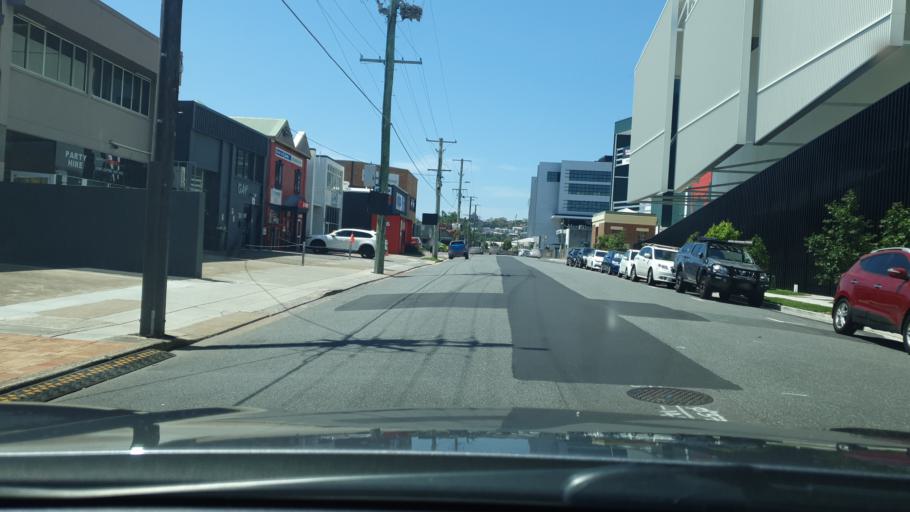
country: AU
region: Queensland
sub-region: Brisbane
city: Windsor
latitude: -27.4432
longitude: 153.0427
